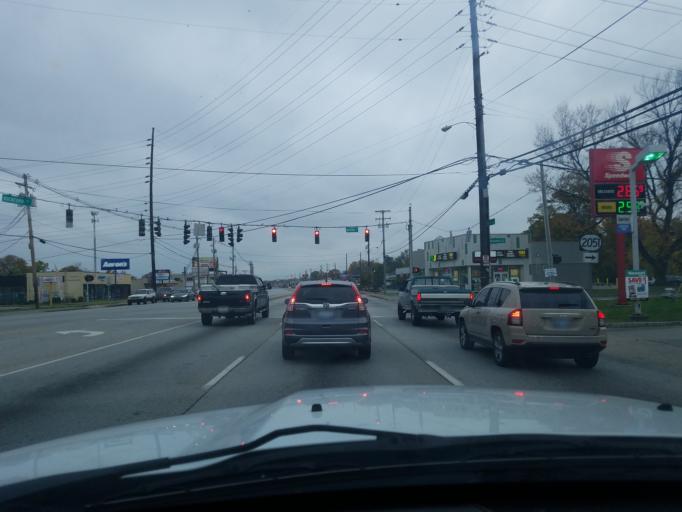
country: US
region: Kentucky
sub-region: Jefferson County
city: Shively
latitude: 38.1746
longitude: -85.8232
